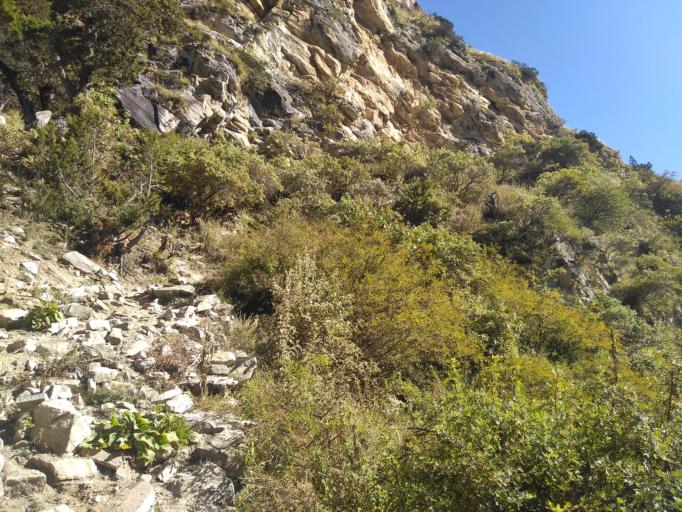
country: NP
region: Western Region
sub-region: Dhawalagiri Zone
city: Jomsom
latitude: 28.9346
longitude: 83.0470
